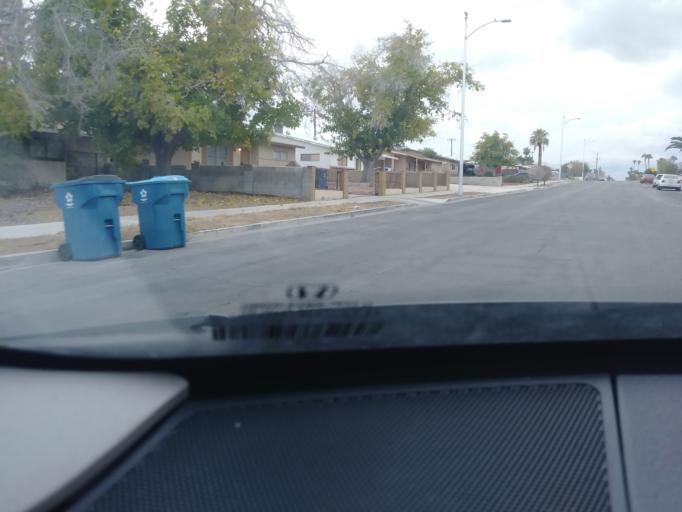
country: US
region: Nevada
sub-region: Clark County
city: Spring Valley
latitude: 36.1631
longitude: -115.2155
